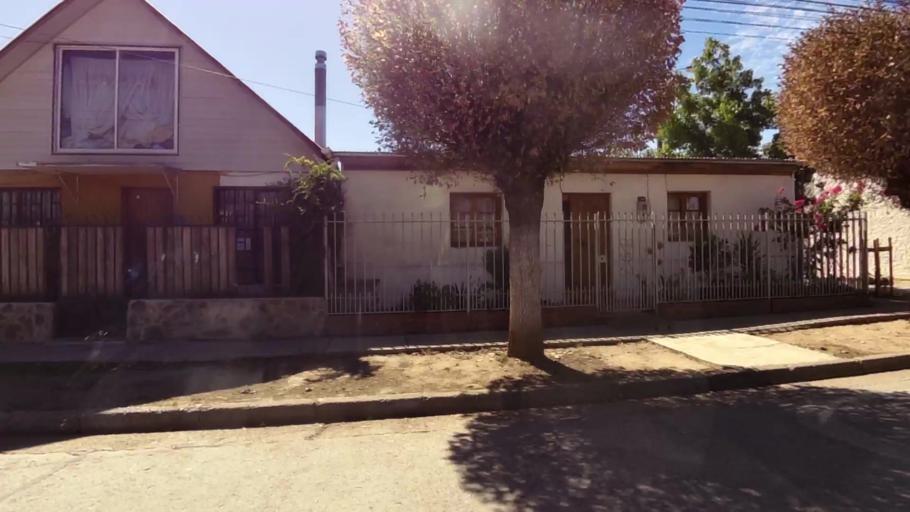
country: CL
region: O'Higgins
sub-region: Provincia de Cachapoal
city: Graneros
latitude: -33.9724
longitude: -70.7104
